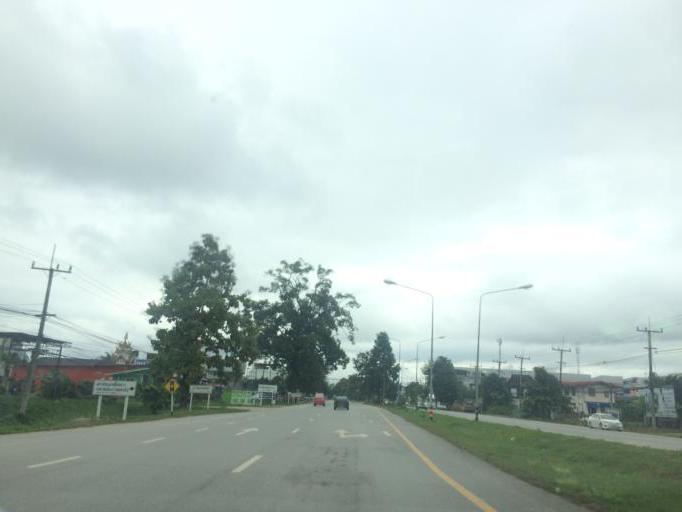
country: TH
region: Chiang Rai
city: Chiang Rai
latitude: 19.8591
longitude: 99.8182
